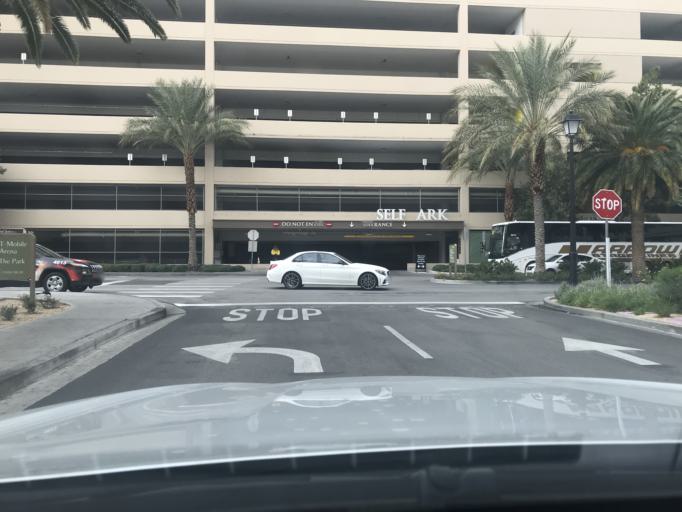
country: US
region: Nevada
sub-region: Clark County
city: Paradise
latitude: 36.1046
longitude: -115.1772
